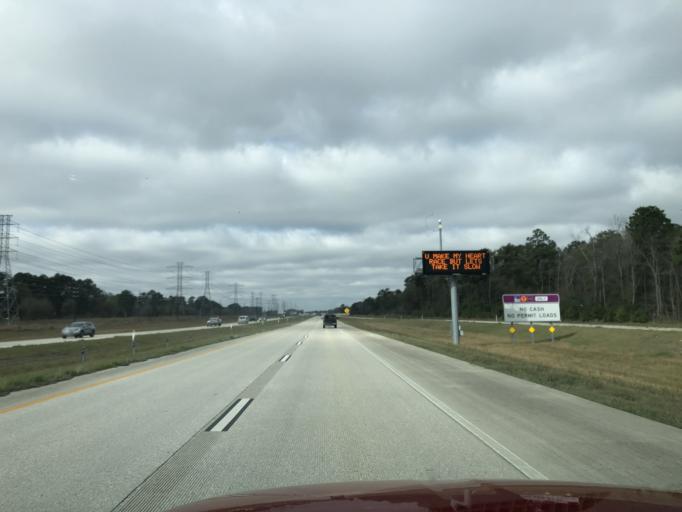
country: US
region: Texas
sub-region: Harris County
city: Spring
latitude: 30.0903
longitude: -95.4633
